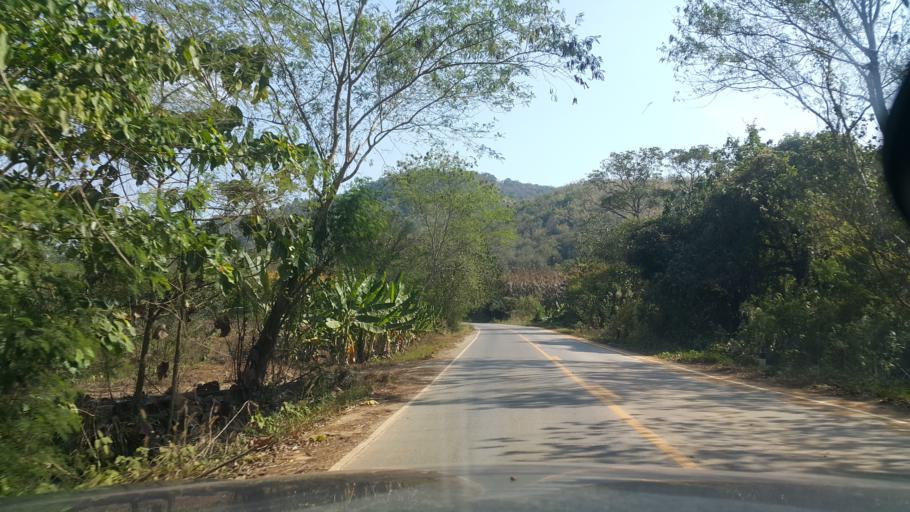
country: TH
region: Loei
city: Pak Chom
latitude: 18.1004
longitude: 102.0365
